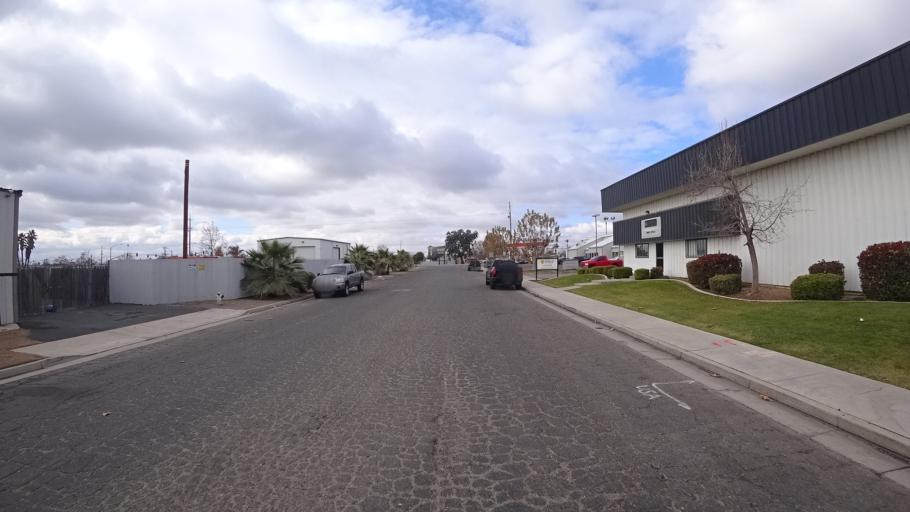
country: US
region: California
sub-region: Kern County
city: Bakersfield
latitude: 35.3332
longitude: -119.0016
